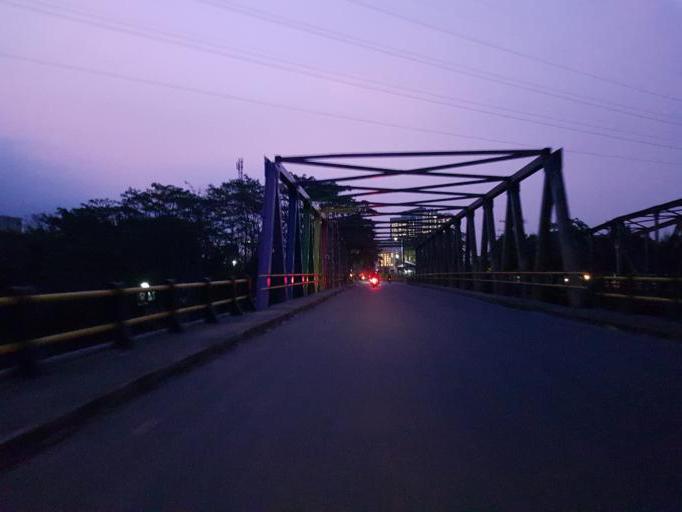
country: ID
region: West Java
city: Serpong
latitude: -6.3114
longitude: 106.6585
